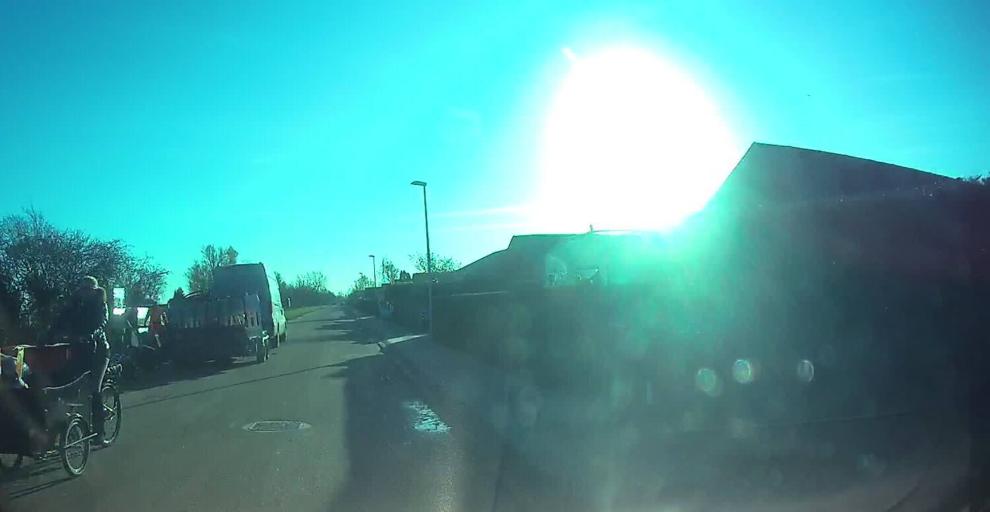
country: DK
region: Capital Region
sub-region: Tarnby Kommune
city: Tarnby
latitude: 55.5972
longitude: 12.5885
